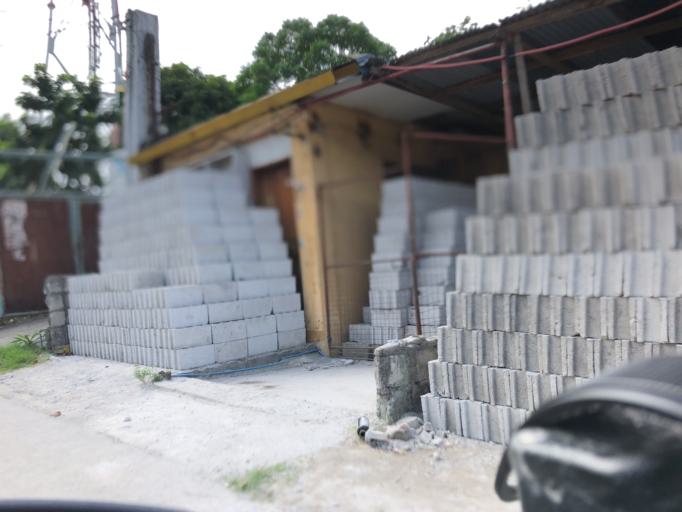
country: PH
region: Central Luzon
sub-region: Province of Bulacan
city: San Jose del Monte
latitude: 14.7601
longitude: 121.0511
